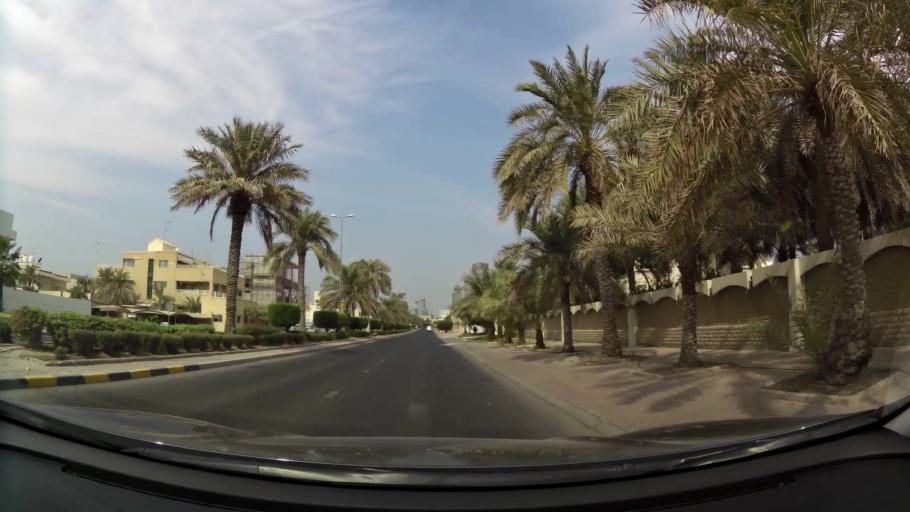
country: KW
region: Al Asimah
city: Ash Shamiyah
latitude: 29.3491
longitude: 47.9794
